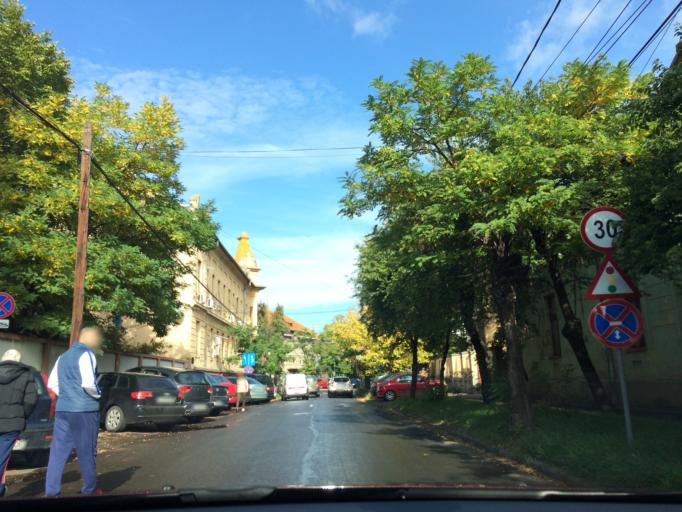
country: RO
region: Timis
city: Timisoara
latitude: 45.7438
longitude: 21.2304
